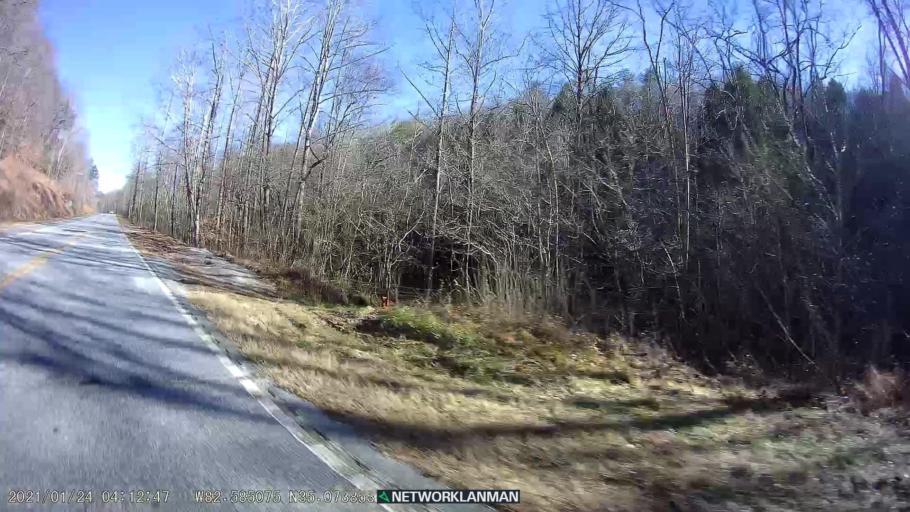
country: US
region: South Carolina
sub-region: Greenville County
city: Slater-Marietta
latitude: 35.0739
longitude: -82.5848
